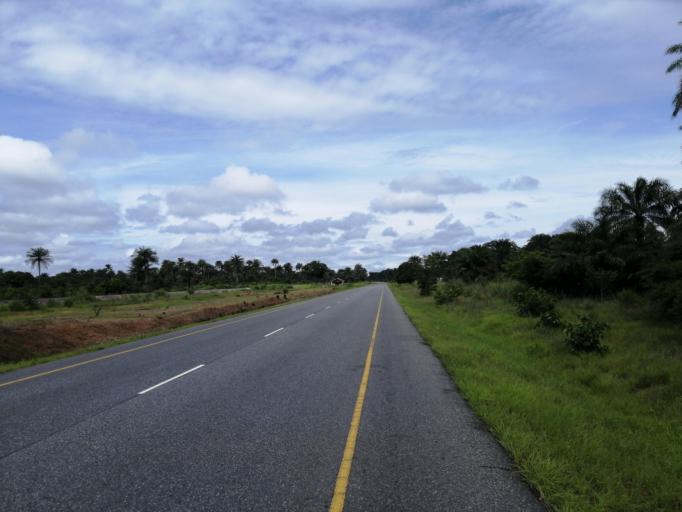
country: SL
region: Northern Province
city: Pepel
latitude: 8.7250
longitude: -12.9547
